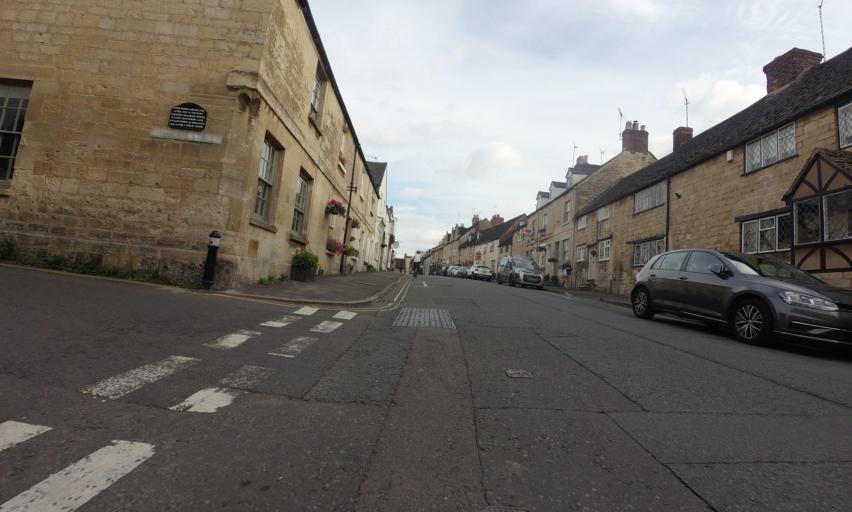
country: GB
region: England
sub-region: Gloucestershire
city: Winchcombe
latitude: 51.9548
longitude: -1.9654
